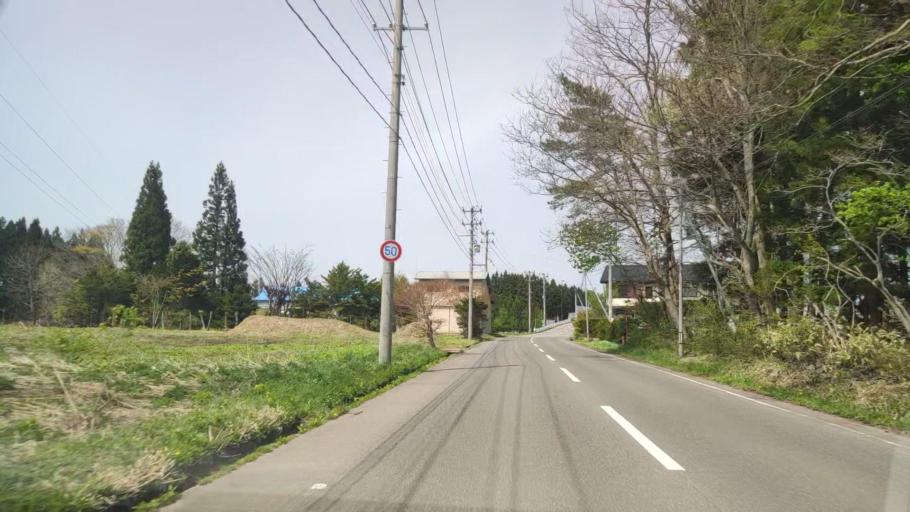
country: JP
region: Aomori
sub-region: Misawa Shi
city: Inuotose
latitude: 40.7225
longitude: 141.1414
